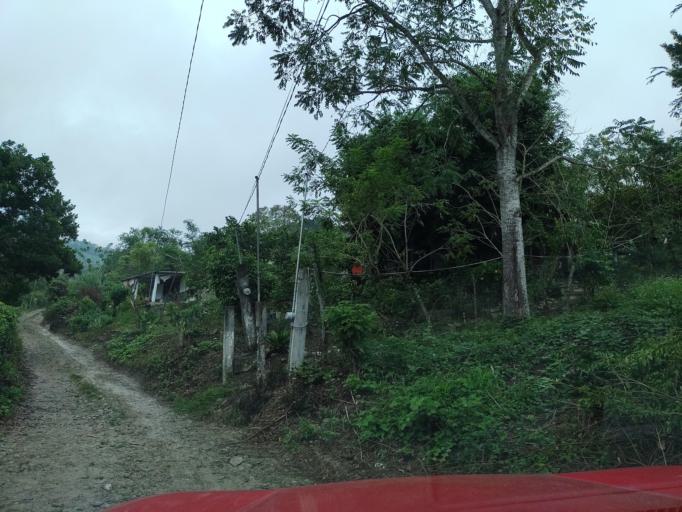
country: MX
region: Puebla
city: Espinal
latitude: 20.2631
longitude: -97.3694
